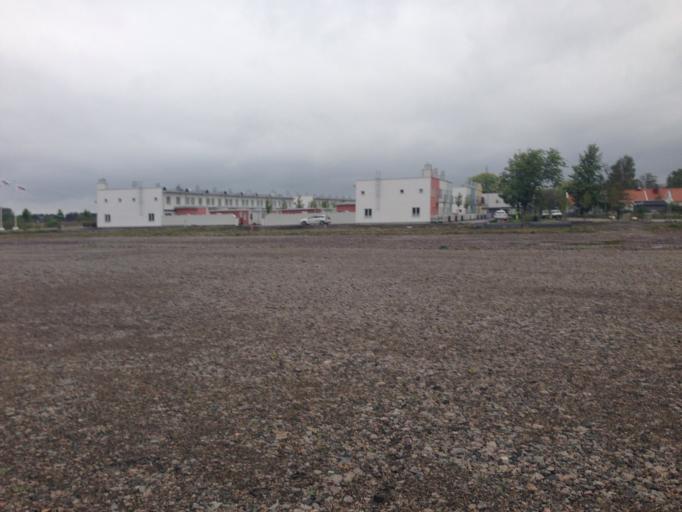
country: SE
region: Skane
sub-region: Lomma Kommun
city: Lomma
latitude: 55.6785
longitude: 13.0681
